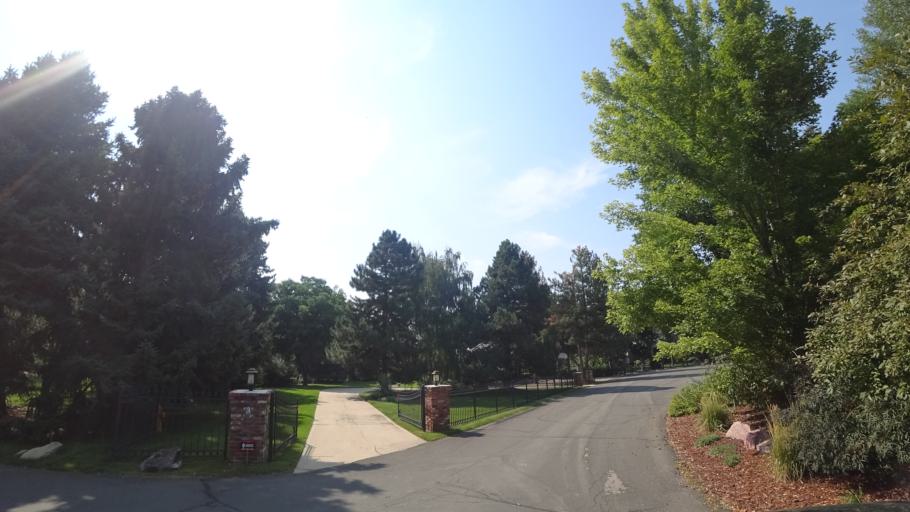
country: US
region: Colorado
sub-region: Arapahoe County
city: Greenwood Village
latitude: 39.6216
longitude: -104.9610
